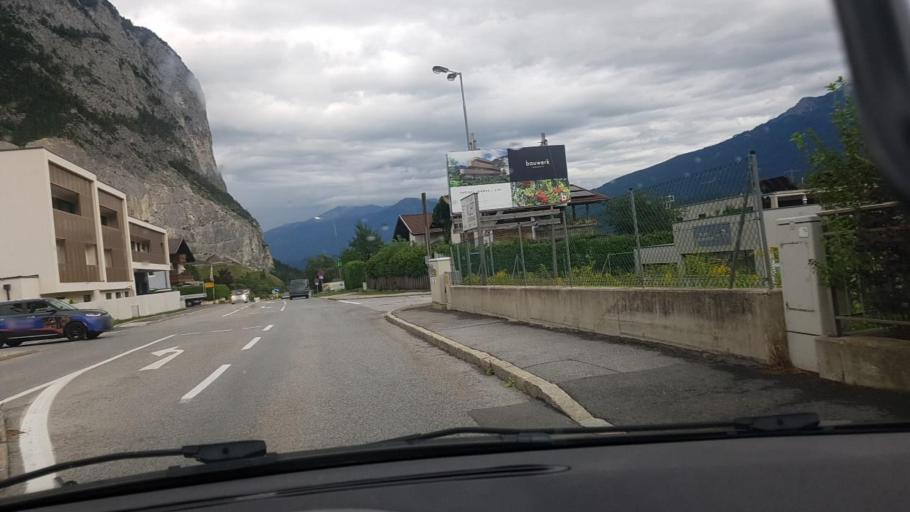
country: AT
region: Tyrol
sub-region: Politischer Bezirk Innsbruck Land
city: Unterperfuss
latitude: 47.2710
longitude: 11.2530
